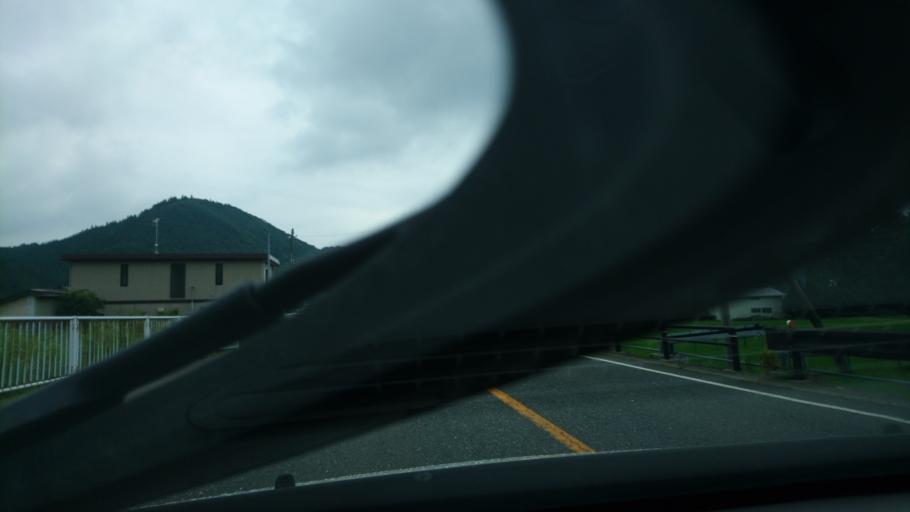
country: JP
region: Miyagi
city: Furukawa
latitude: 38.7280
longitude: 140.7956
